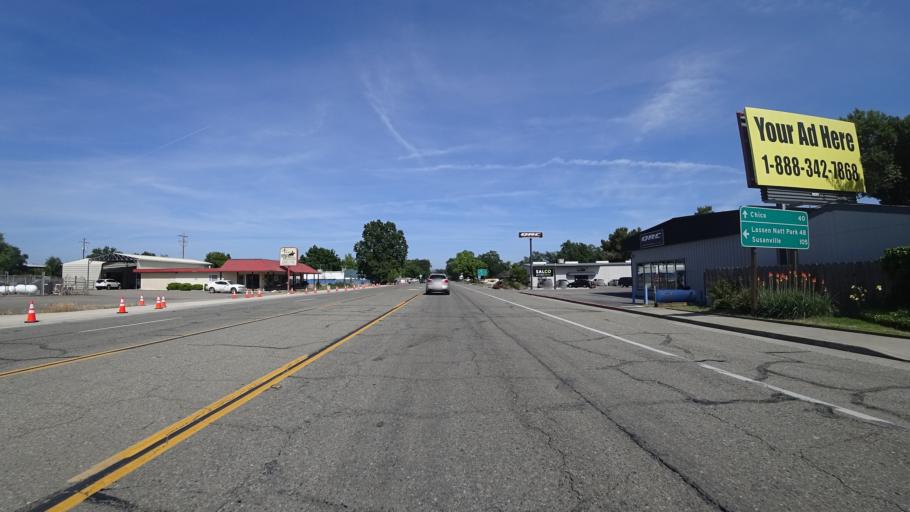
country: US
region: California
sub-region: Tehama County
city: Red Bluff
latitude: 40.1857
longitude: -122.1887
